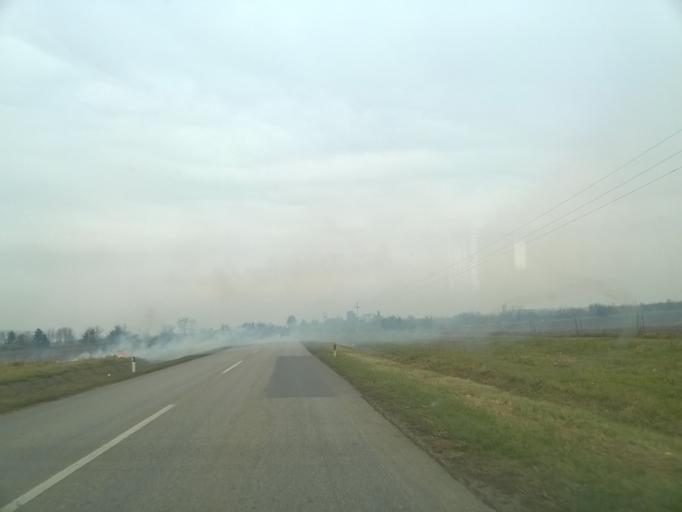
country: RS
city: Crepaja
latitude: 44.9930
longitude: 20.6421
